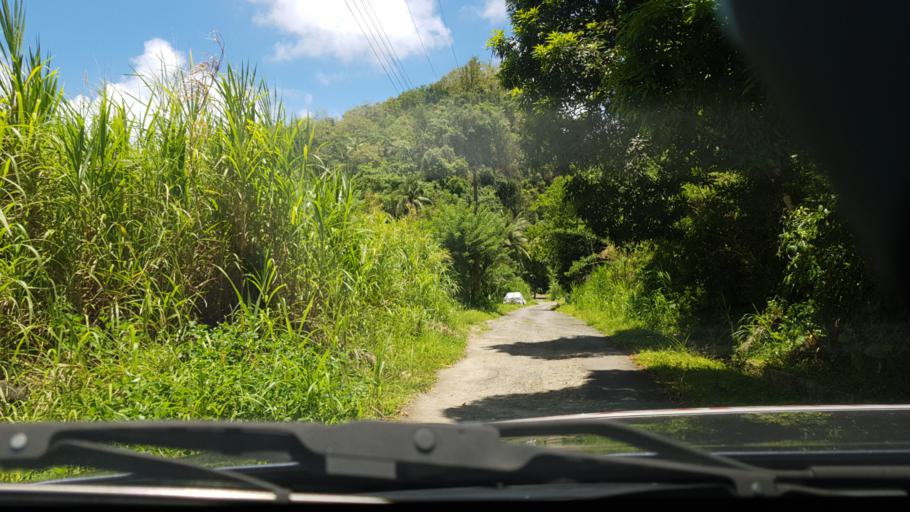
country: LC
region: Anse-la-Raye
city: Canaries
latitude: 13.8991
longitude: -61.0590
